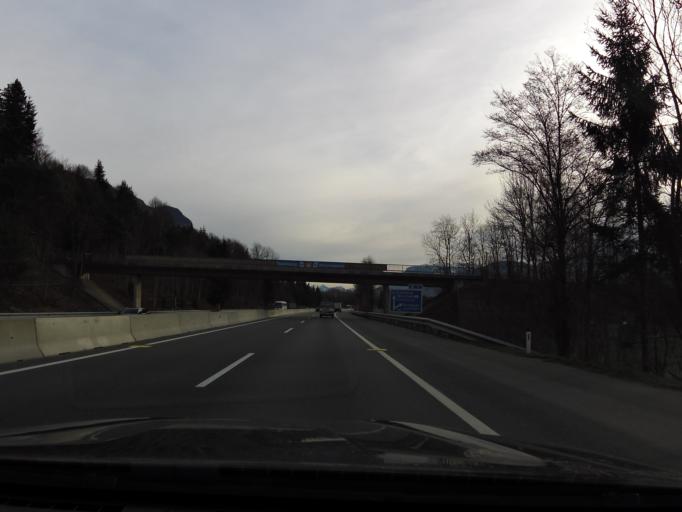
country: AT
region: Tyrol
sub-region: Politischer Bezirk Kufstein
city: Langkampfen
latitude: 47.5287
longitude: 12.0783
